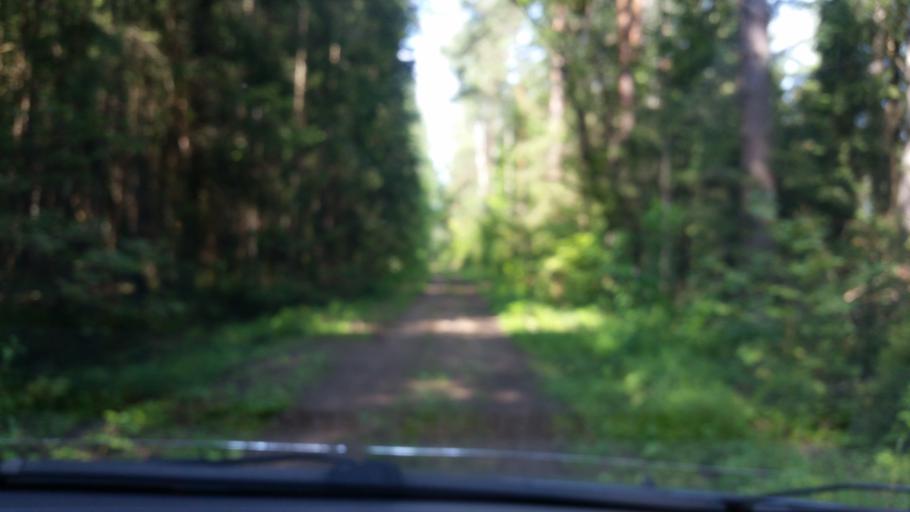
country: RU
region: Moskovskaya
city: Bol'shoye Gryzlovo
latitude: 54.9087
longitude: 37.7584
